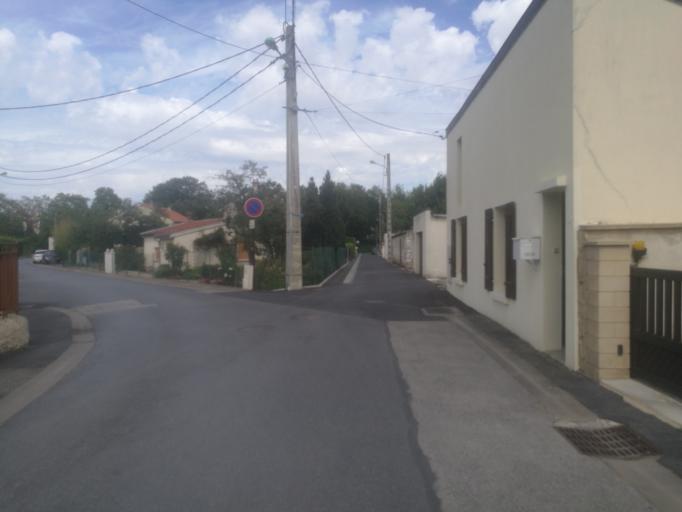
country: FR
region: Champagne-Ardenne
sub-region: Departement de la Marne
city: Compertrix
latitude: 48.9597
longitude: 4.3497
